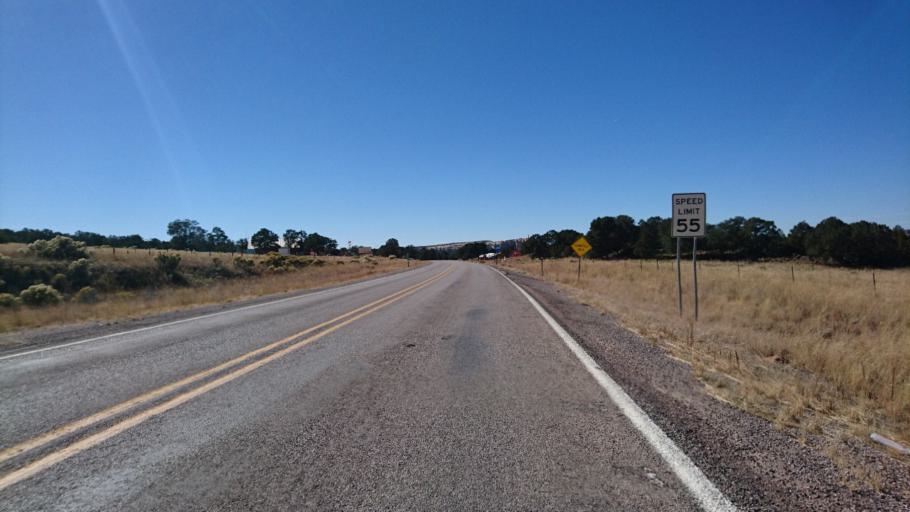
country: US
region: New Mexico
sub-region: McKinley County
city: Thoreau
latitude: 35.0450
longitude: -108.3173
